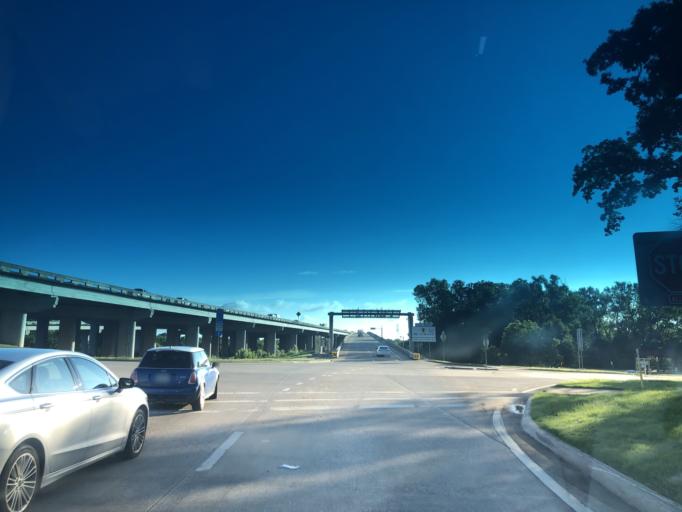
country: US
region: Texas
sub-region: Dallas County
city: Grand Prairie
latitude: 32.7784
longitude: -97.0254
